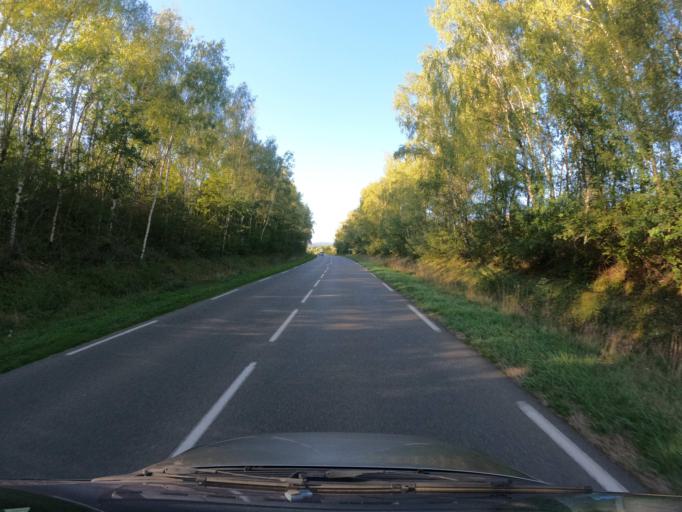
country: FR
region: Bourgogne
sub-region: Departement de Saone-et-Loire
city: Montchanin
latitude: 46.7428
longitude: 4.4448
